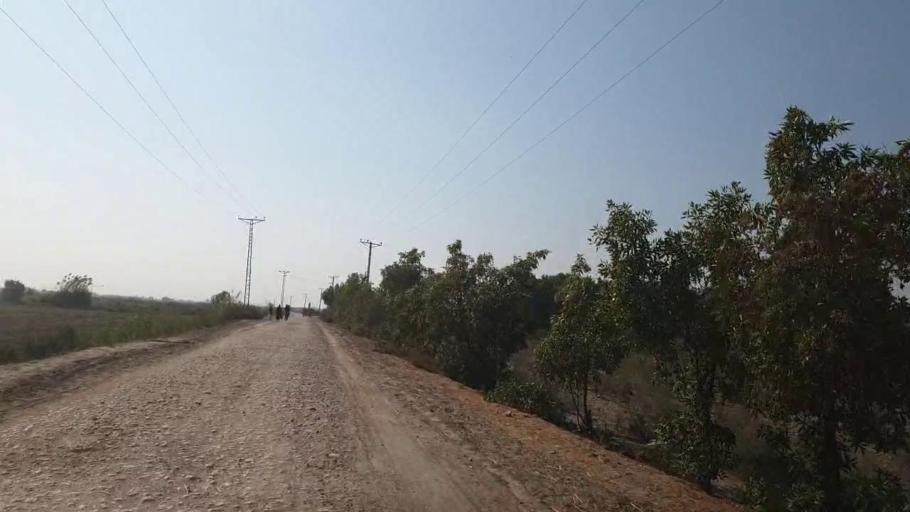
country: PK
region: Sindh
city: Thatta
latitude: 24.7392
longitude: 67.7945
